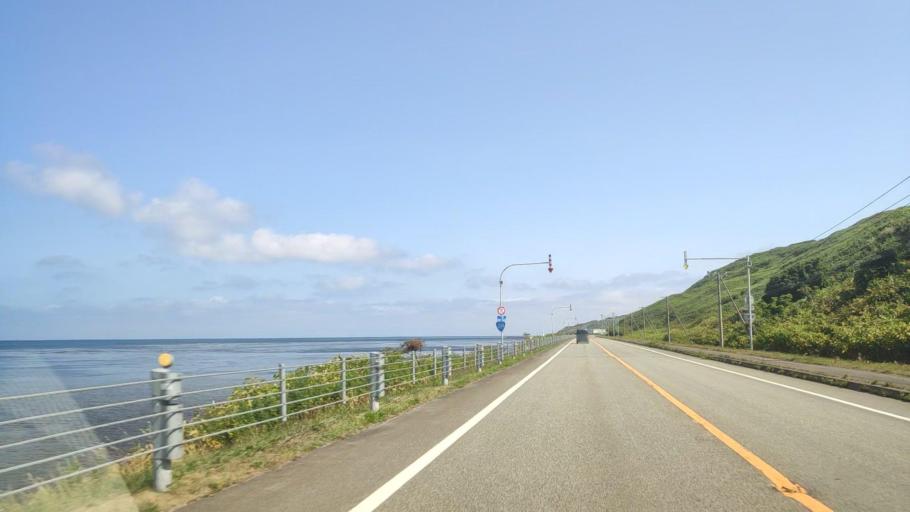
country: JP
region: Hokkaido
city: Makubetsu
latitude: 45.4738
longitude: 141.8740
